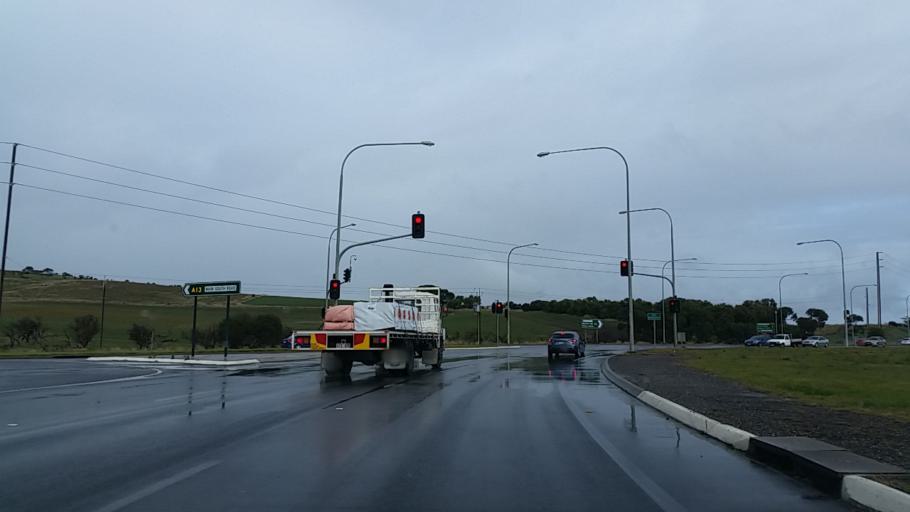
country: AU
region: South Australia
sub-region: Onkaparinga
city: Noarlunga Downs
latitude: -35.1652
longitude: 138.5086
